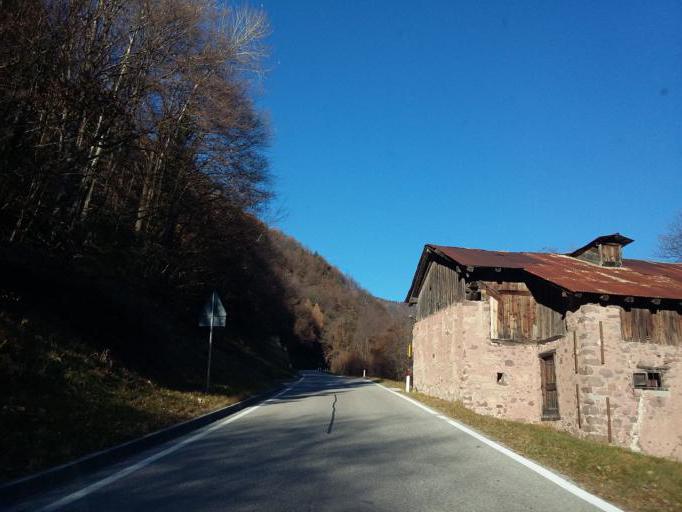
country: IT
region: Trentino-Alto Adige
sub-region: Provincia di Trento
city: Brione
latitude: 45.8954
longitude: 10.5966
